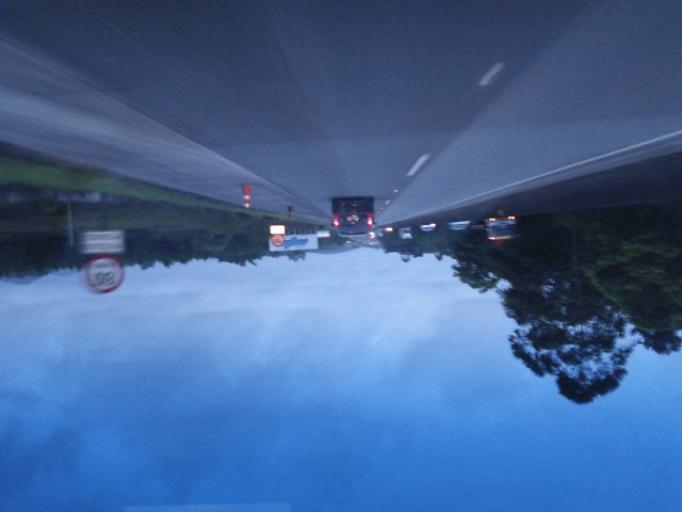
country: BR
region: Santa Catarina
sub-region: Barra Velha
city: Barra Velha
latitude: -26.6113
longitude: -48.7218
